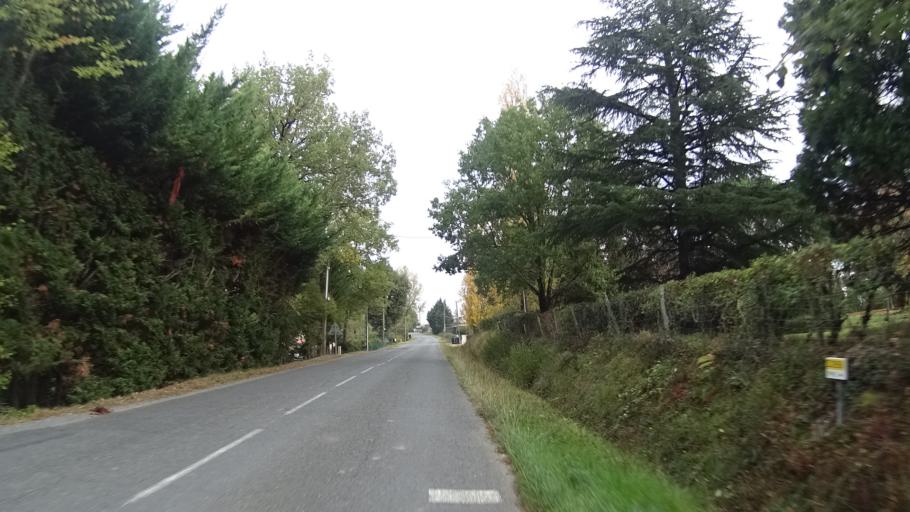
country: FR
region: Aquitaine
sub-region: Departement du Lot-et-Garonne
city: Estillac
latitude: 44.1217
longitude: 0.5950
